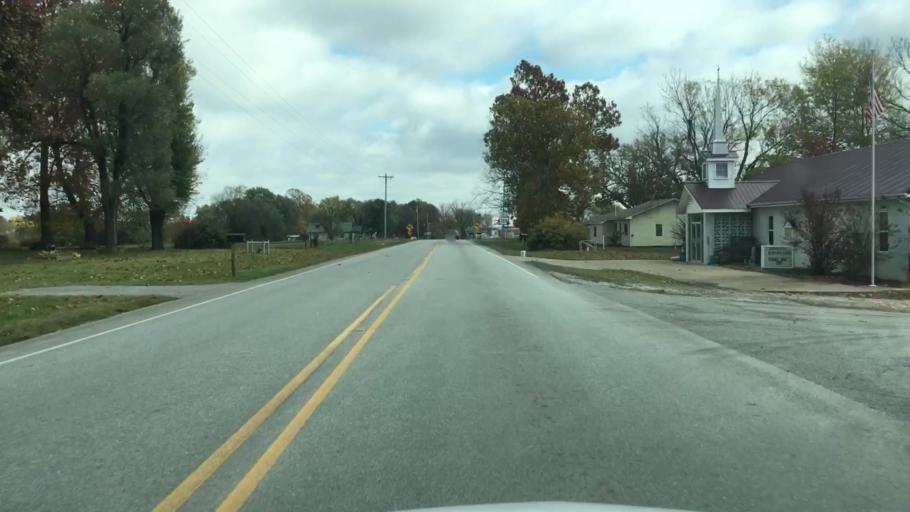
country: US
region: Arkansas
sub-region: Benton County
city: Centerton
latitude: 36.2616
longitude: -94.3552
